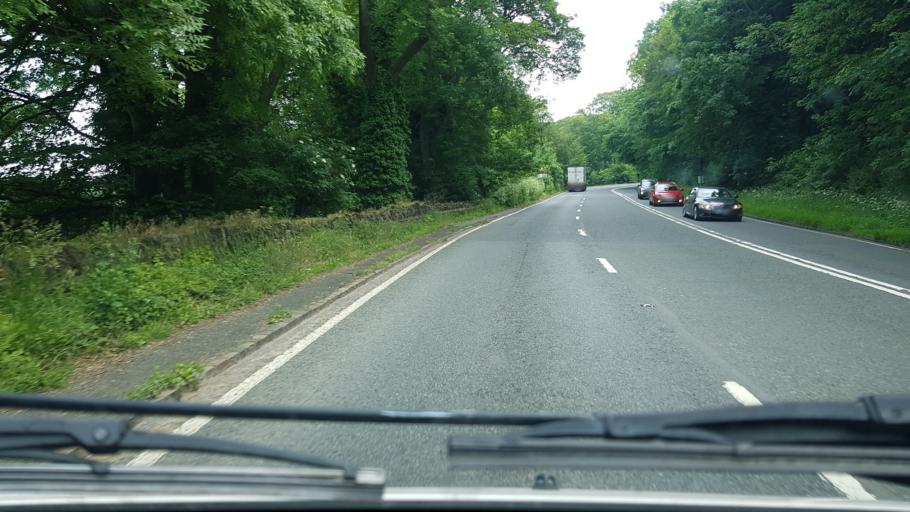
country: GB
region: England
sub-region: Worcestershire
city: Broadway
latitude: 52.0338
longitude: -1.8350
